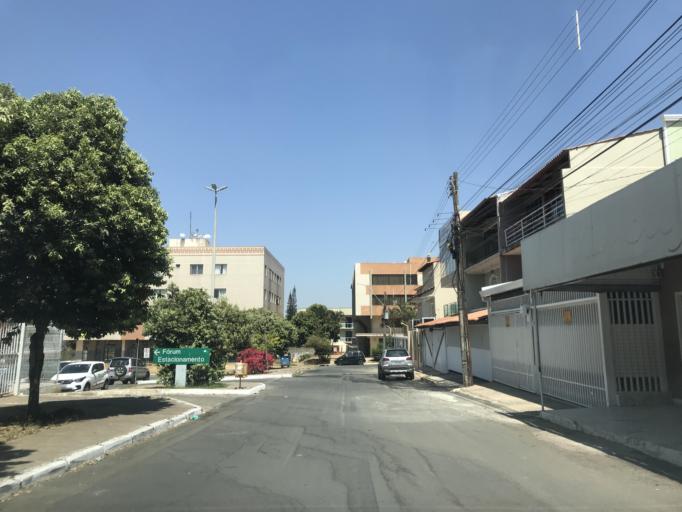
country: BR
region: Federal District
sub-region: Brasilia
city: Brasilia
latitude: -15.8823
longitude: -48.0115
